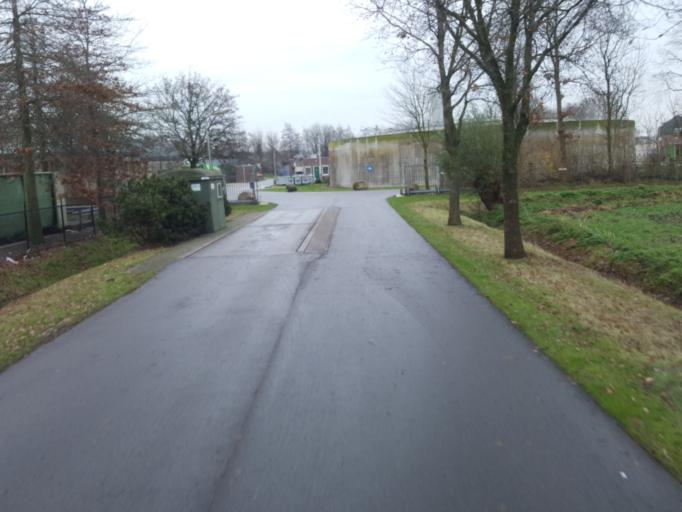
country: NL
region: Gelderland
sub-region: Gemeente Ede
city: Ederveen
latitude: 52.0426
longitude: 5.6042
